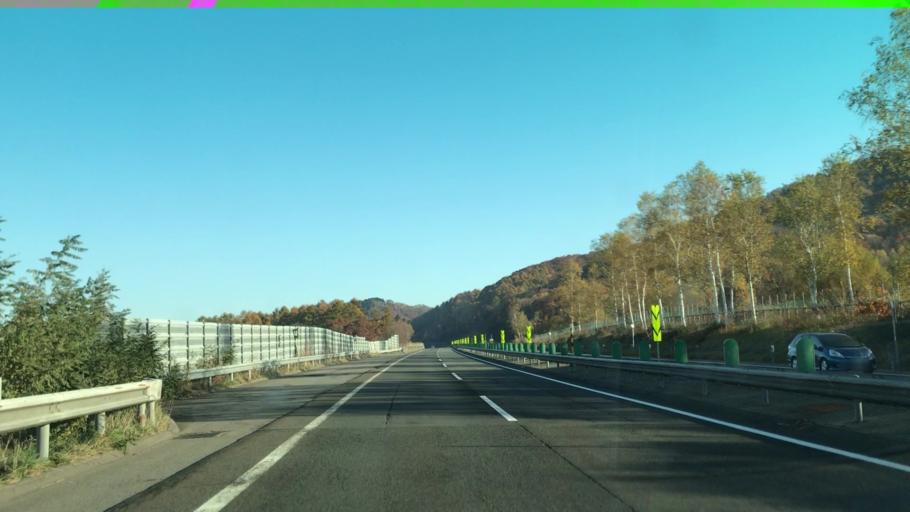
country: JP
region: Hokkaido
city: Sunagawa
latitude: 43.4056
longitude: 141.9056
